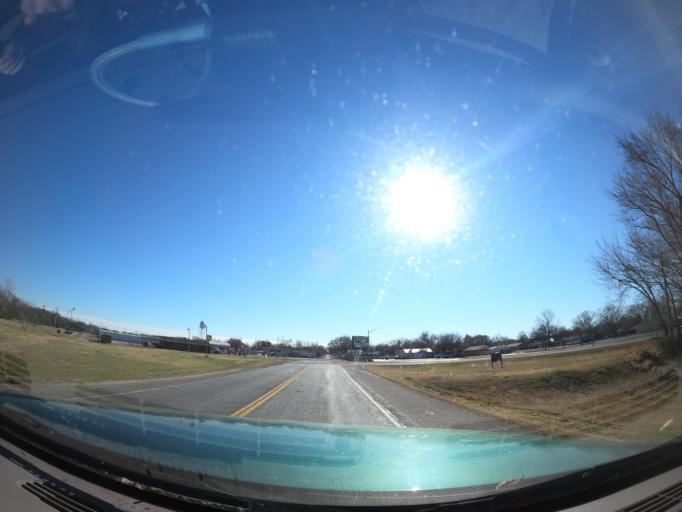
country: US
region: Oklahoma
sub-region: Muskogee County
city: Haskell
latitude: 35.8247
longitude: -95.6775
